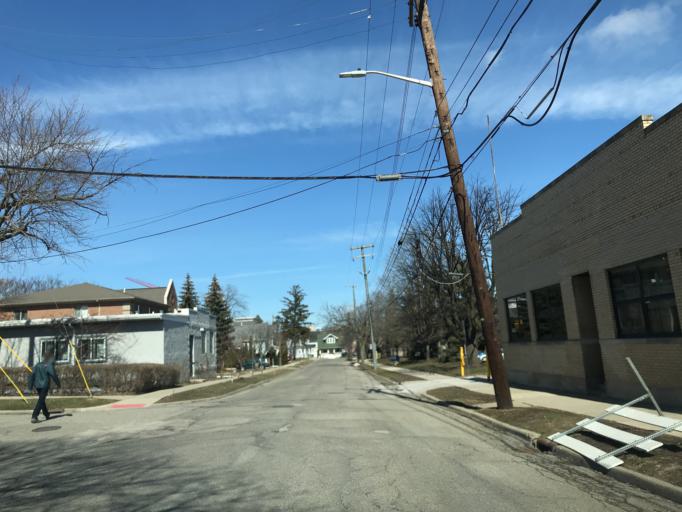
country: US
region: Michigan
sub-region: Washtenaw County
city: Ann Arbor
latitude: 42.2701
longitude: -83.7475
